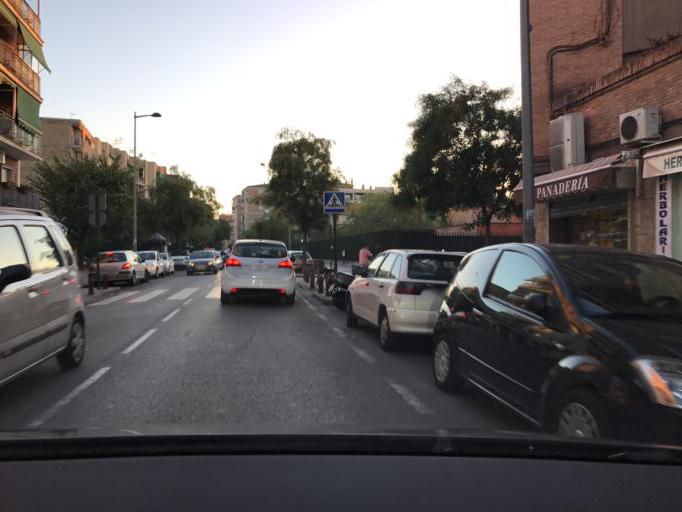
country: ES
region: Andalusia
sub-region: Provincia de Granada
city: Armilla
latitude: 37.1578
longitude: -3.6021
